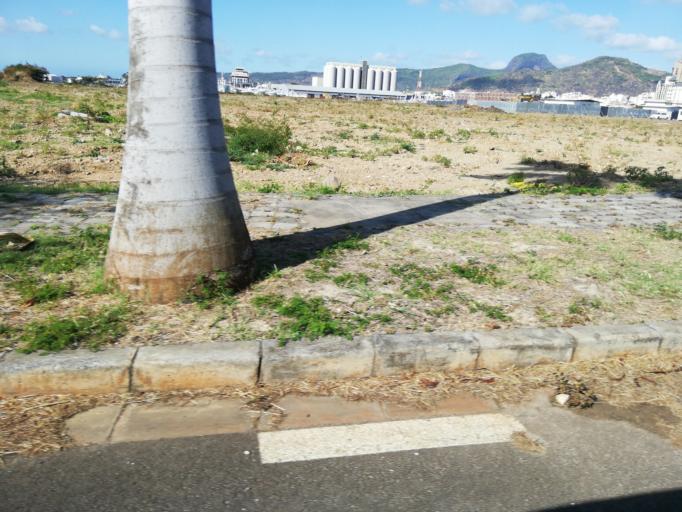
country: MU
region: Port Louis
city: Port Louis
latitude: -20.1589
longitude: 57.4925
